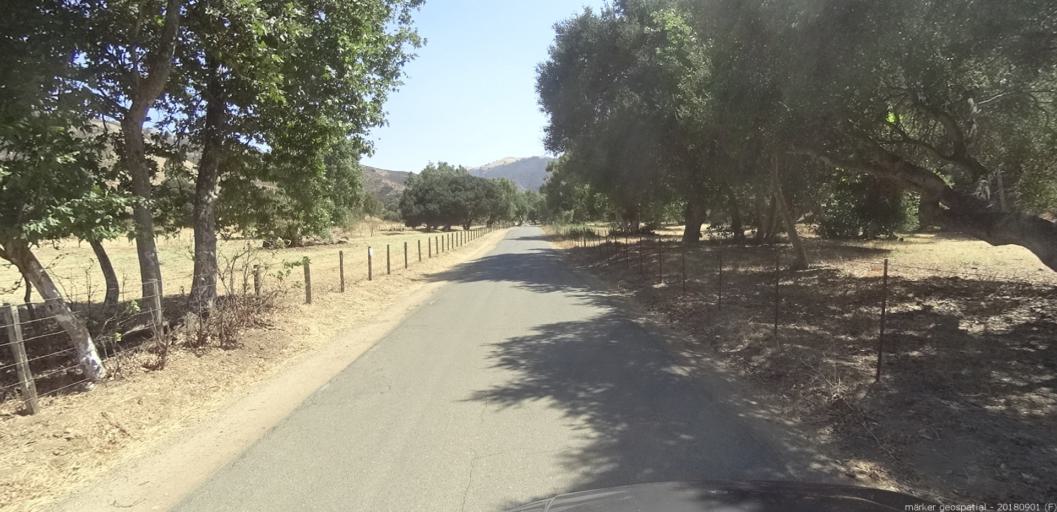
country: US
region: California
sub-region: Monterey County
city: Gonzales
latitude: 36.6032
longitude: -121.4205
